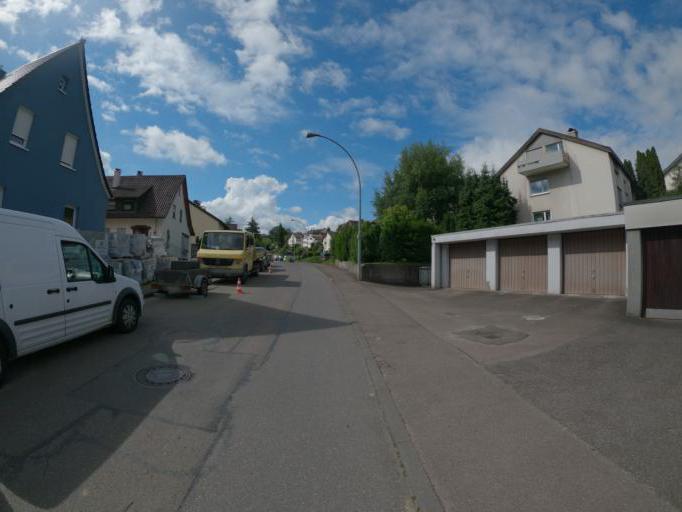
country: DE
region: Baden-Wuerttemberg
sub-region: Regierungsbezirk Stuttgart
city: Ebersbach an der Fils
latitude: 48.7097
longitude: 9.5242
